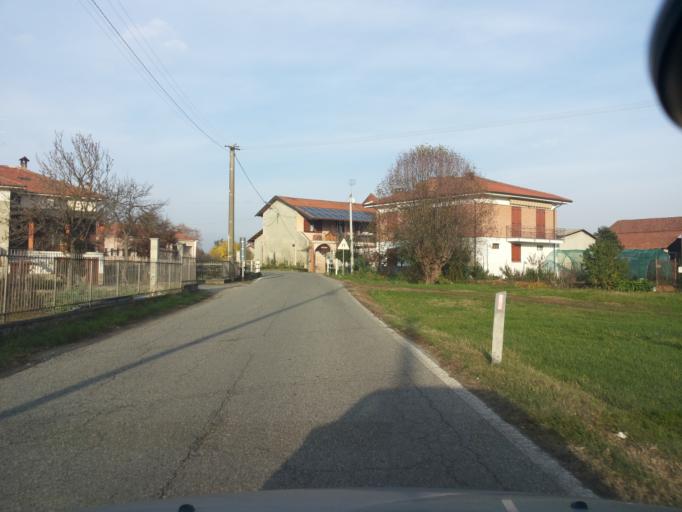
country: IT
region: Piedmont
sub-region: Provincia di Biella
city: Salussola
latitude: 45.4573
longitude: 8.1159
